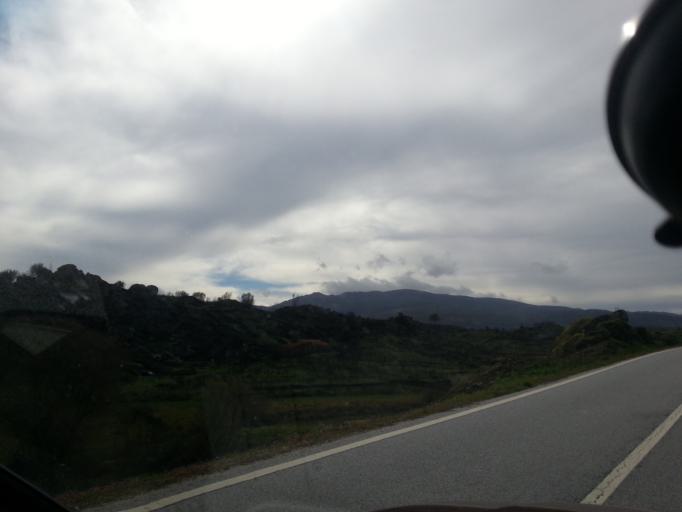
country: PT
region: Guarda
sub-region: Fornos de Algodres
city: Fornos de Algodres
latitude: 40.5604
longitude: -7.5611
